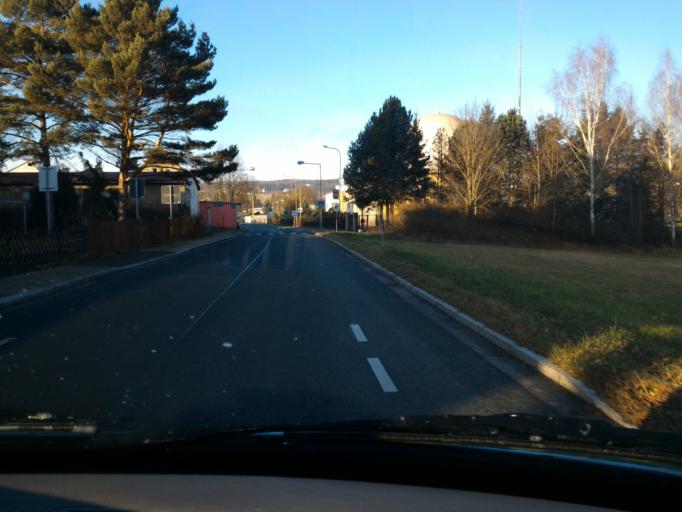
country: CZ
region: Ustecky
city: Varnsdorf
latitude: 50.9043
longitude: 14.6504
